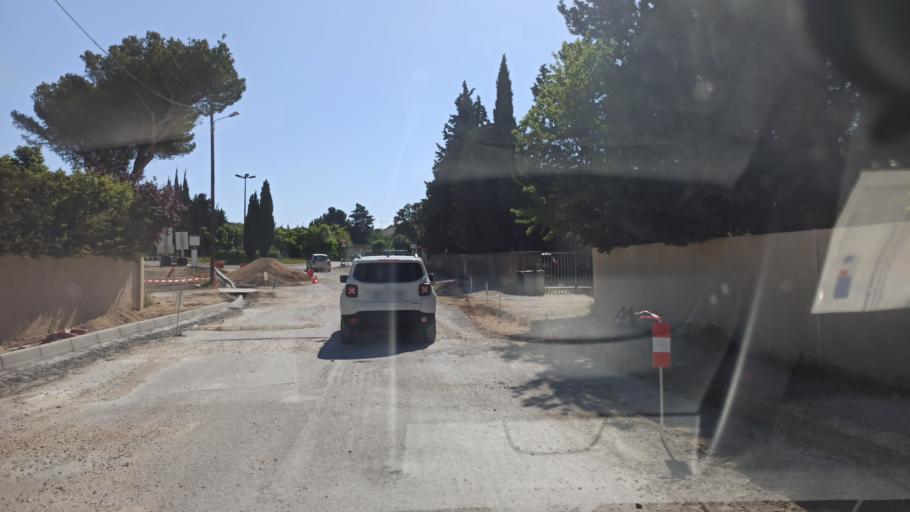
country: FR
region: Languedoc-Roussillon
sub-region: Departement du Gard
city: Les Angles
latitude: 43.9649
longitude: 4.7688
